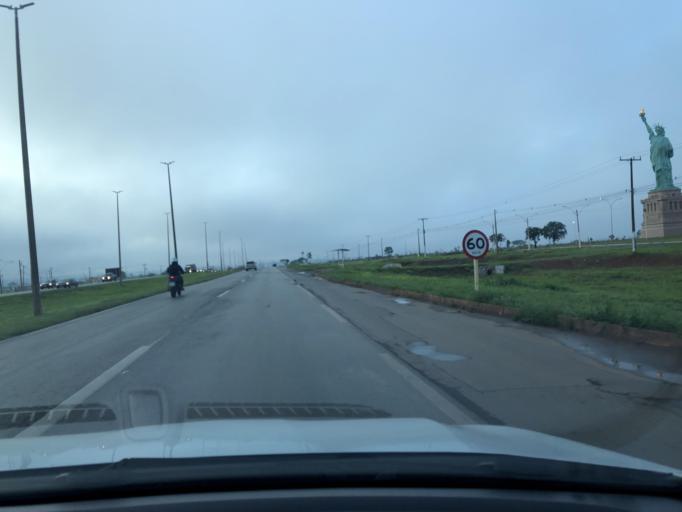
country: BR
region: Goias
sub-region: Luziania
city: Luziania
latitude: -16.0955
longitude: -47.9808
